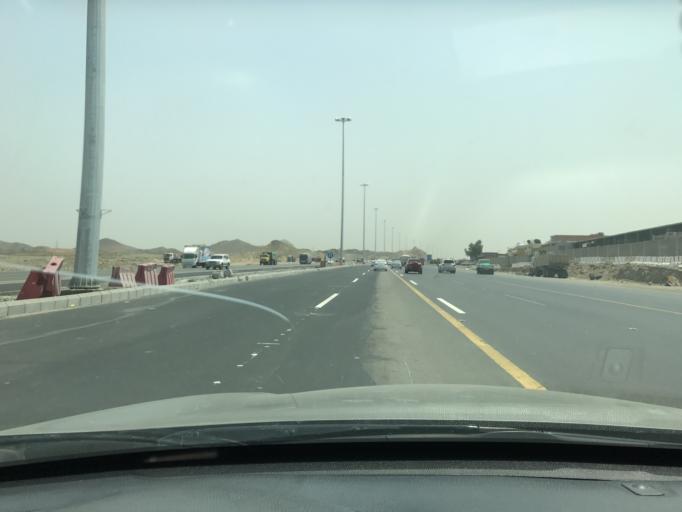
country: SA
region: Makkah
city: Jeddah
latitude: 21.6147
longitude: 39.2467
